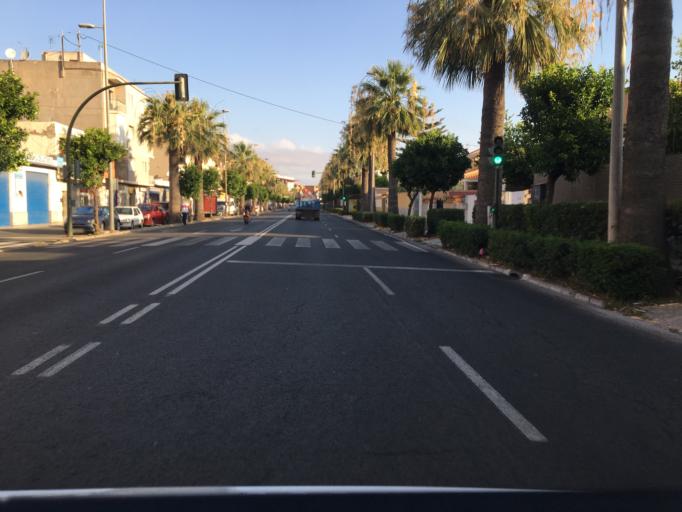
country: ES
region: Murcia
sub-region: Murcia
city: Cartagena
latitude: 37.6241
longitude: -0.9998
